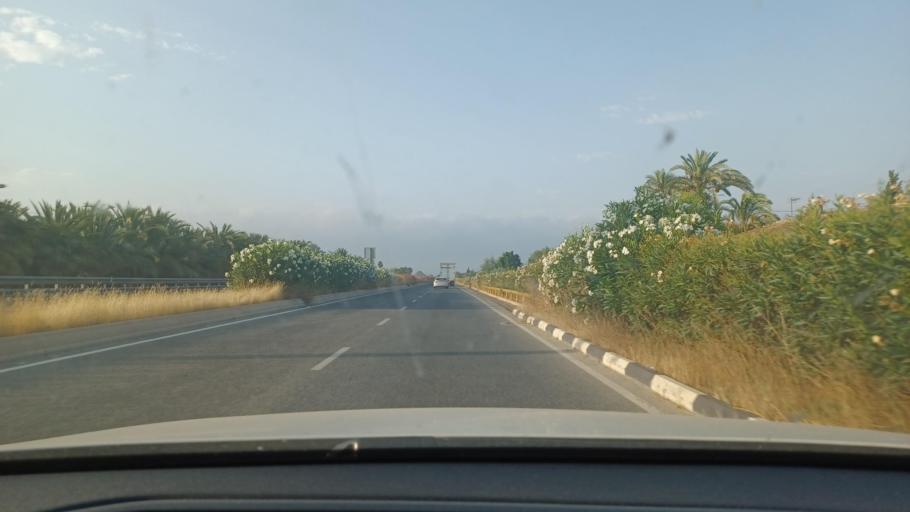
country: ES
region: Valencia
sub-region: Provincia de Alicante
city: Elche
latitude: 38.1864
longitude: -0.7014
